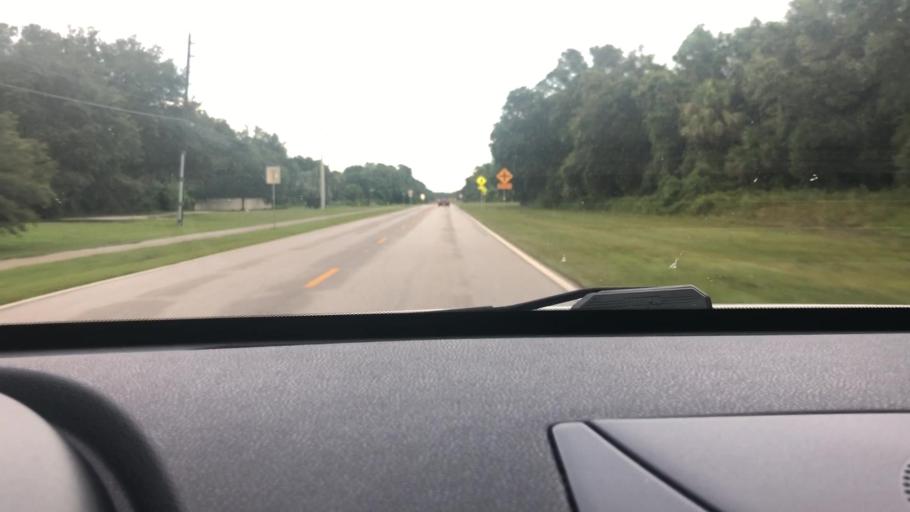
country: US
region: Florida
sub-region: Charlotte County
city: Port Charlotte
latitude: 27.0690
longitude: -82.1143
